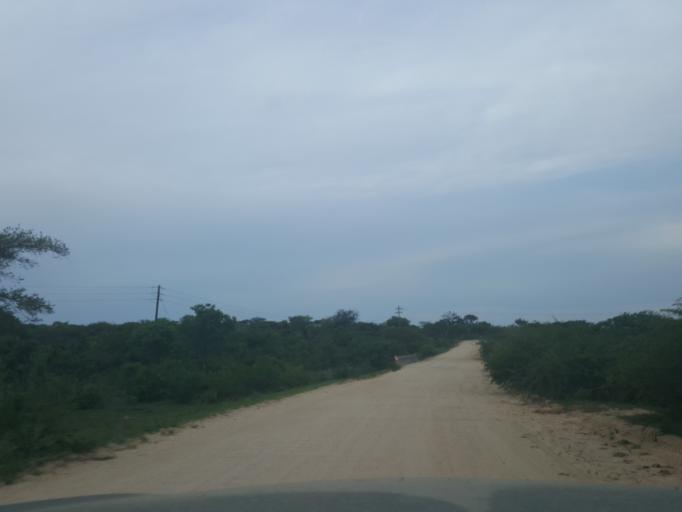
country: ZA
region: Limpopo
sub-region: Mopani District Municipality
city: Hoedspruit
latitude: -24.5728
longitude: 30.9972
